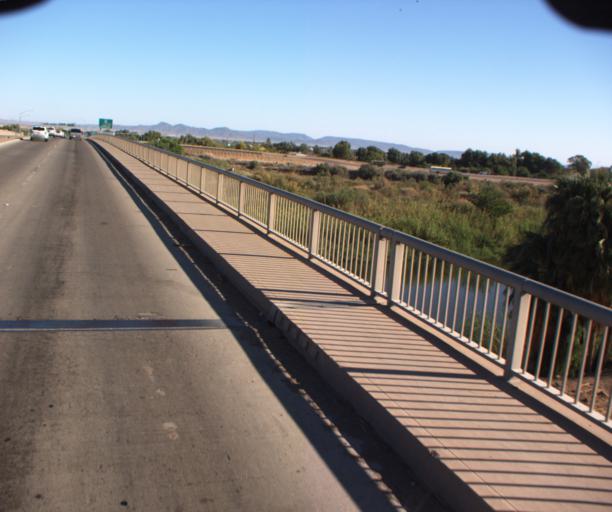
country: US
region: Arizona
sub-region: Yuma County
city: Yuma
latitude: 32.7285
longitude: -114.6245
